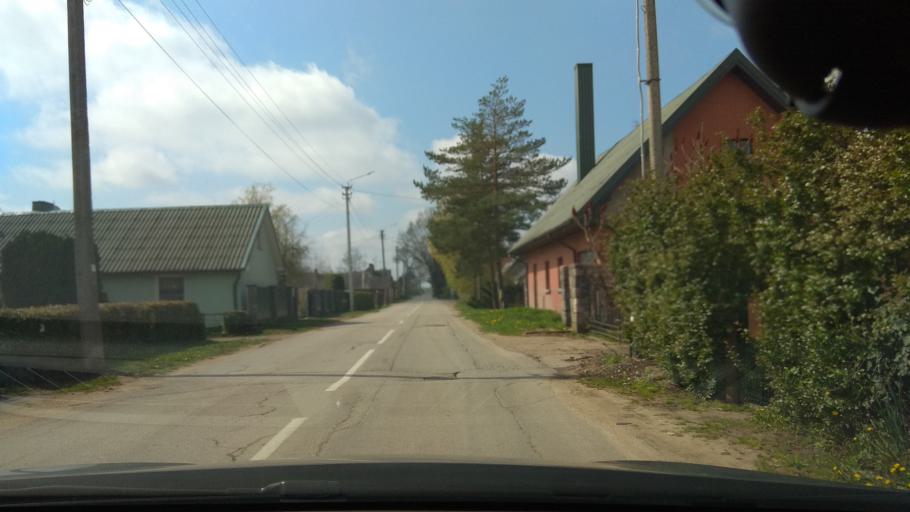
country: LT
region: Siauliu apskritis
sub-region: Joniskis
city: Joniskis
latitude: 56.2454
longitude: 23.6118
